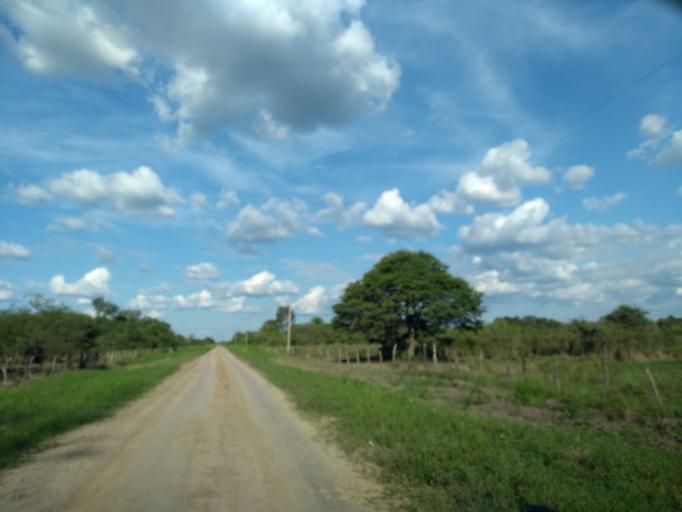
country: AR
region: Chaco
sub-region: Departamento de Quitilipi
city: Quitilipi
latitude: -26.7718
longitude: -60.2012
